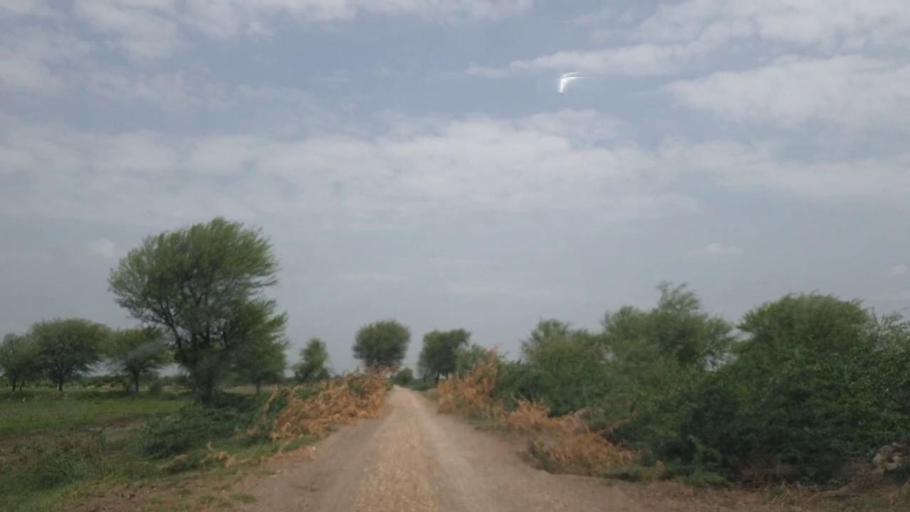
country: PK
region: Sindh
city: Tando Bago
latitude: 24.9254
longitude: 69.0999
